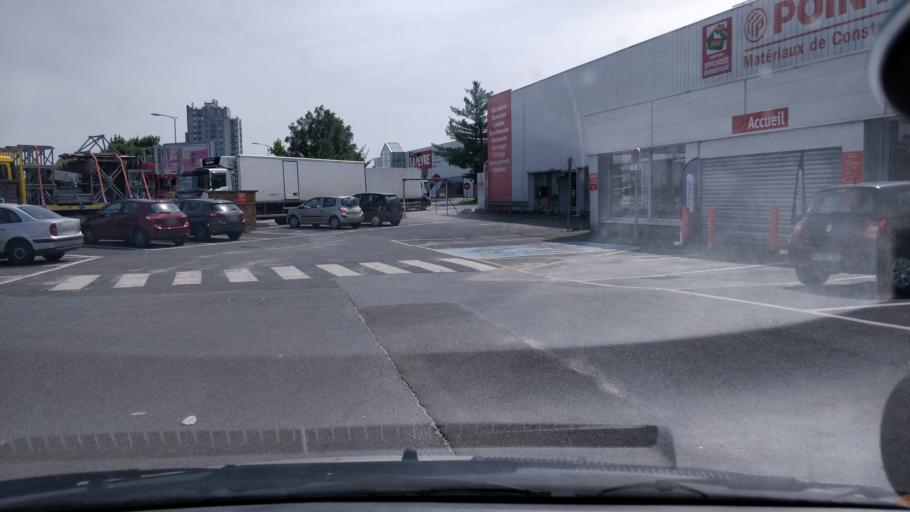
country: FR
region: Ile-de-France
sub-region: Departement de Seine-Saint-Denis
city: Noisy-le-Grand
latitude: 48.8653
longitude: 2.5643
